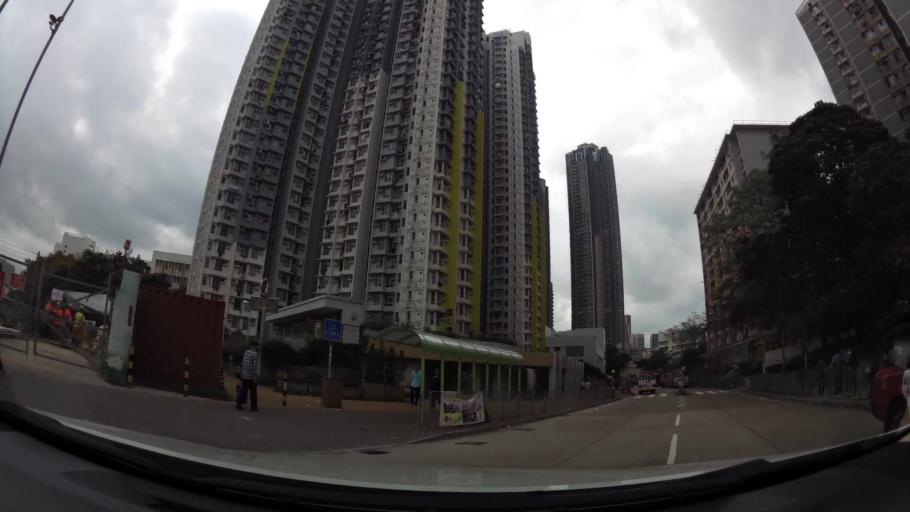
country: HK
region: Kowloon City
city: Kowloon
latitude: 22.3331
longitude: 114.1942
